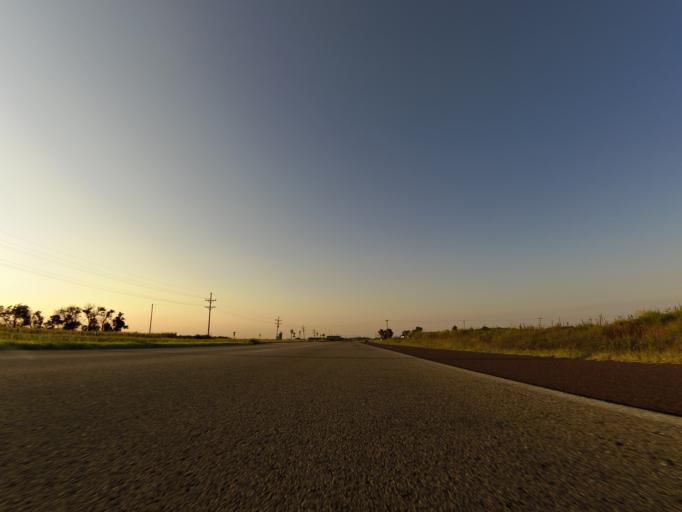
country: US
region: Kansas
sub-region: Reno County
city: South Hutchinson
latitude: 37.9983
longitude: -97.9403
